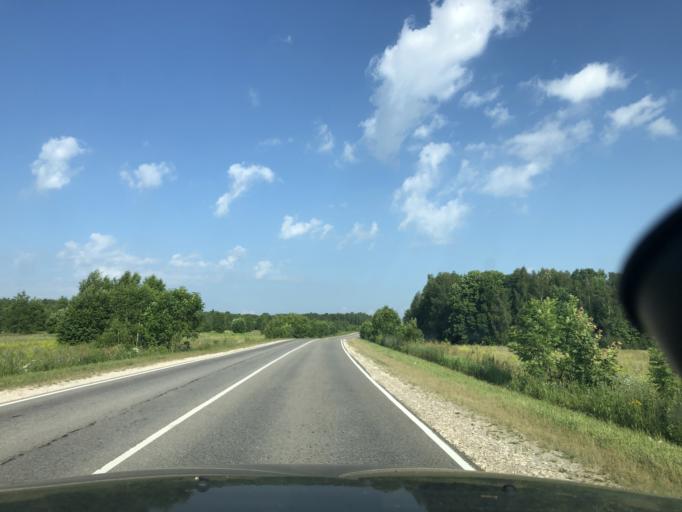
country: RU
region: Tula
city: Dubna
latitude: 54.1328
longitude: 37.0284
